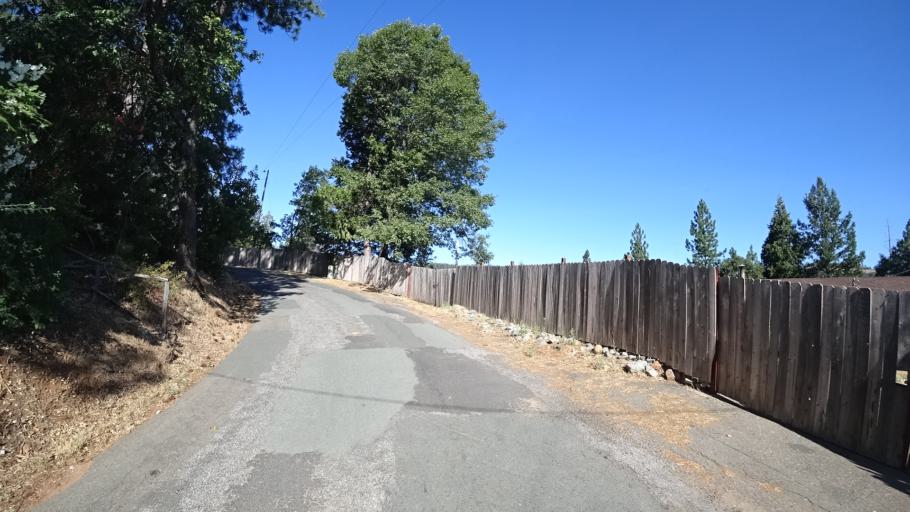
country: US
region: California
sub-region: Amador County
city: Pioneer
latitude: 38.4108
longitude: -120.5610
